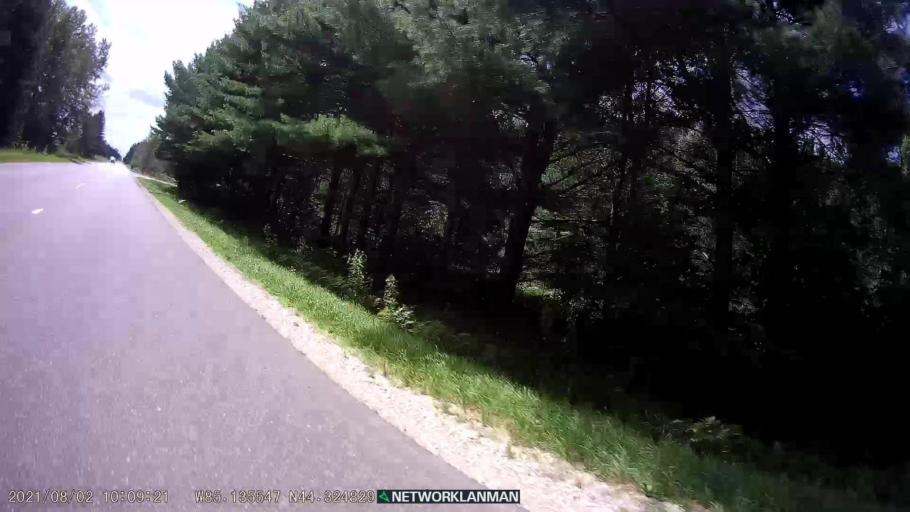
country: US
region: Michigan
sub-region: Missaukee County
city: Lake City
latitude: 44.3245
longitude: -85.1356
